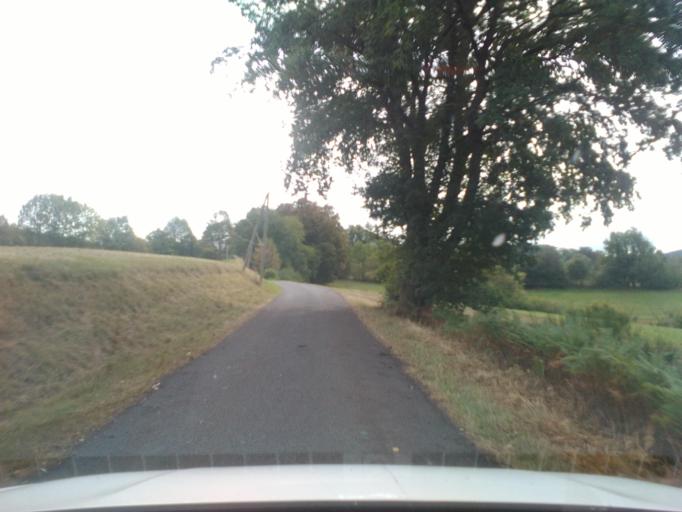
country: FR
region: Lorraine
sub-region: Departement des Vosges
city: Senones
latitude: 48.3601
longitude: 7.0066
